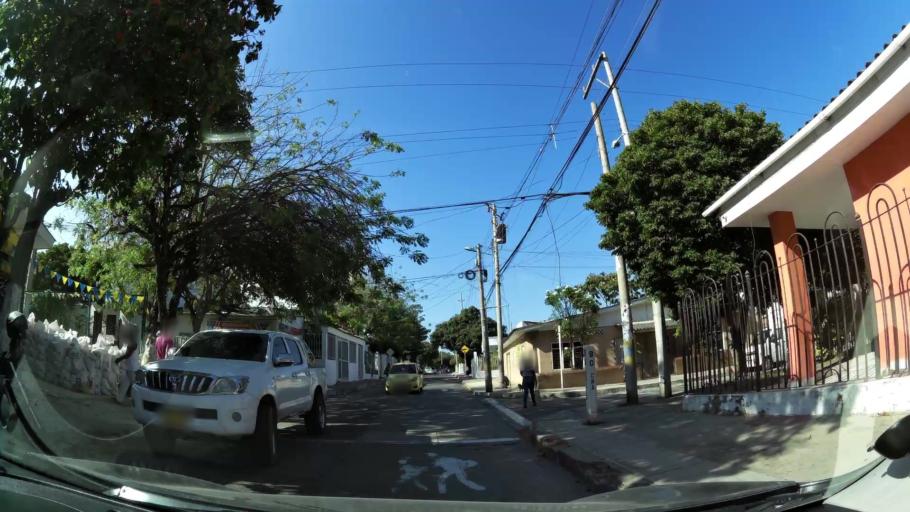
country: CO
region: Atlantico
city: Barranquilla
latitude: 11.0240
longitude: -74.8035
